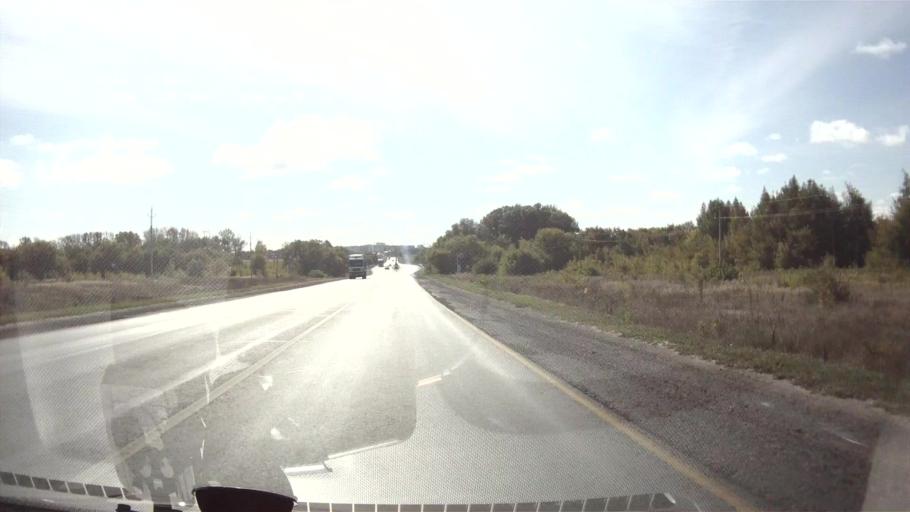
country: RU
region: Ulyanovsk
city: Isheyevka
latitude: 54.3066
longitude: 48.2398
